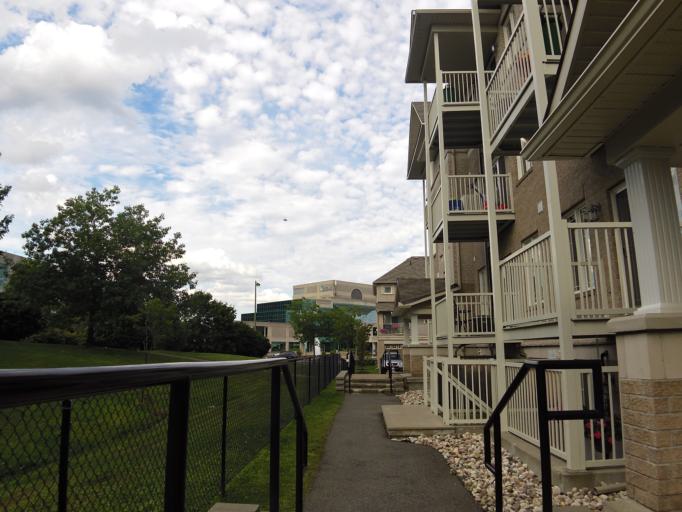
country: CA
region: Ontario
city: Bells Corners
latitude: 45.3436
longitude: -75.7649
